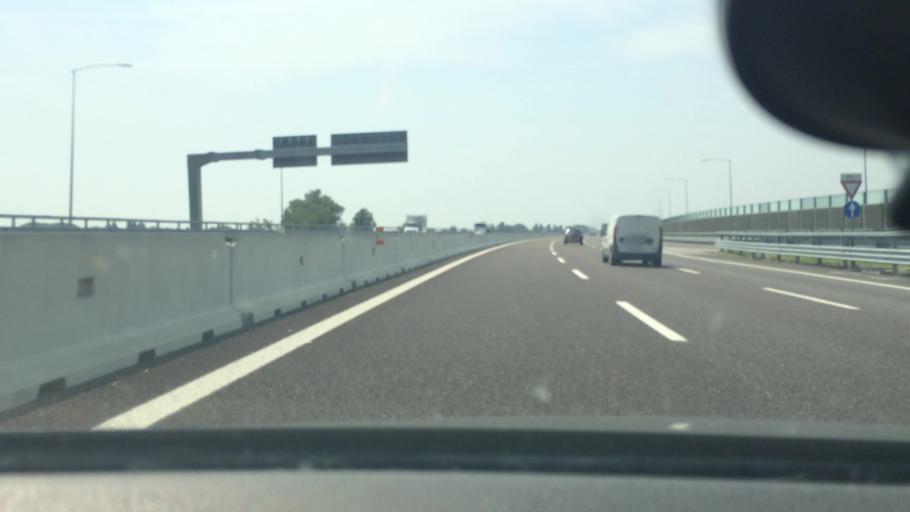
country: IT
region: Lombardy
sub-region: Citta metropolitana di Milano
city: Liscate
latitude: 45.4643
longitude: 9.4340
